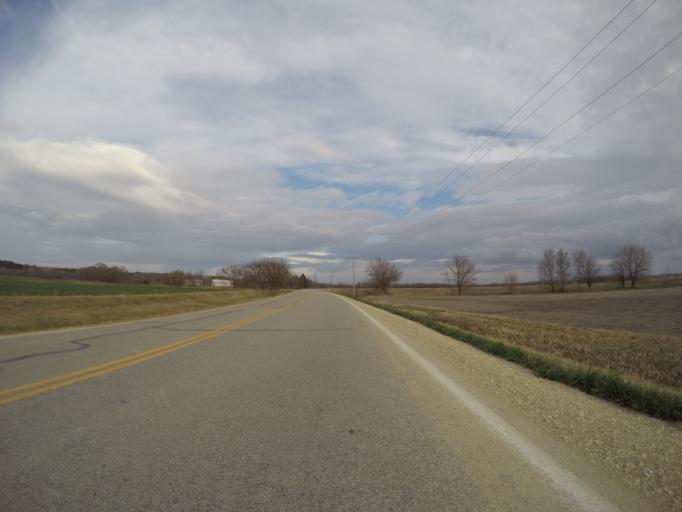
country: US
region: Kansas
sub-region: Riley County
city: Manhattan
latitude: 39.2270
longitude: -96.5619
